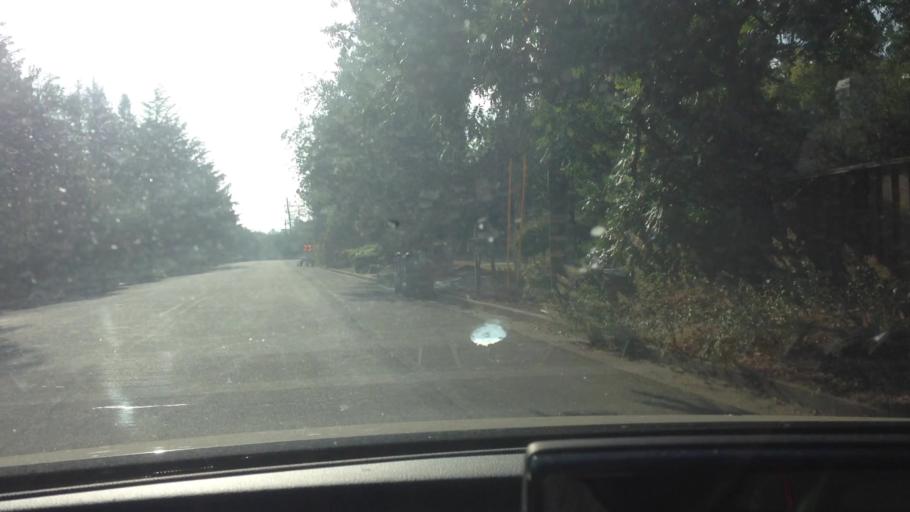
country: US
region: California
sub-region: Santa Clara County
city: Saratoga
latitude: 37.2594
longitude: -122.0176
